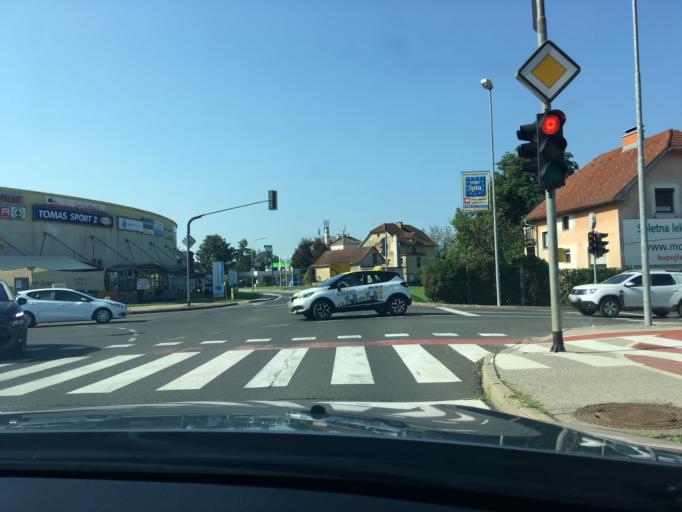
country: SI
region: Novo Mesto
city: Novo Mesto
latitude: 45.8151
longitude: 15.1536
